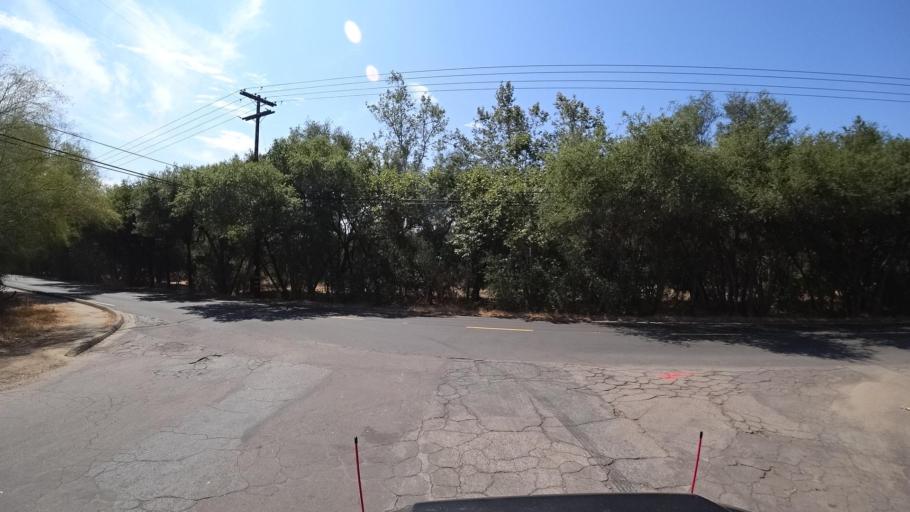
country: US
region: California
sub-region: San Diego County
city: Escondido
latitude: 33.1698
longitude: -117.0950
